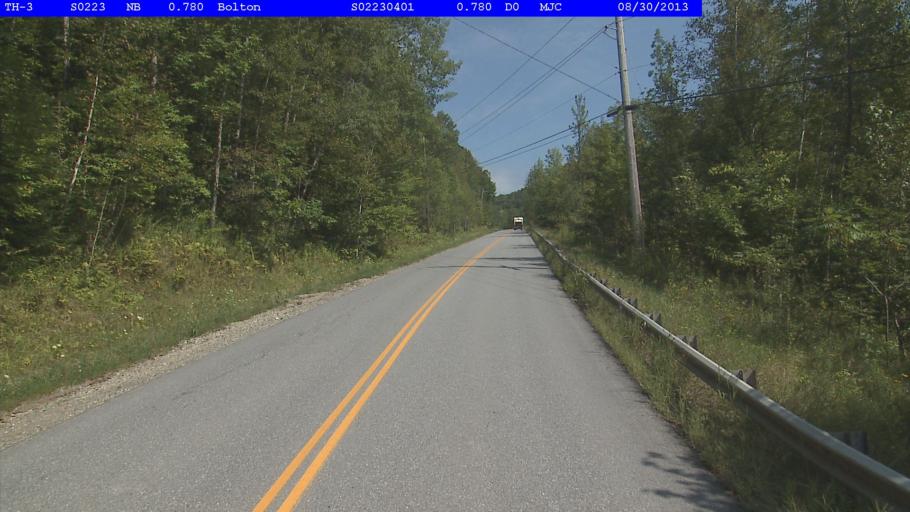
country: US
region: Vermont
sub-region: Washington County
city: Waterbury
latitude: 44.3820
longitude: -72.8751
